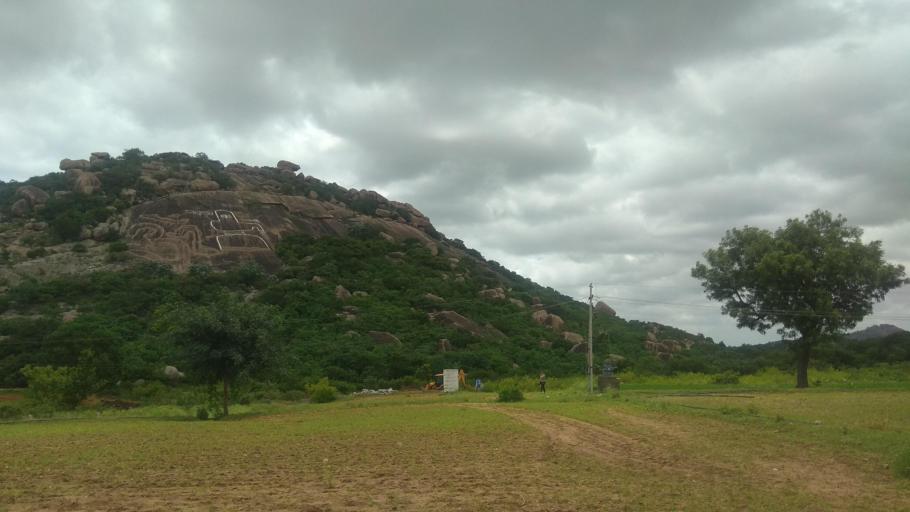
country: IN
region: Telangana
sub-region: Mahbubnagar
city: Farrukhnagar
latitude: 16.8885
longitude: 78.5014
